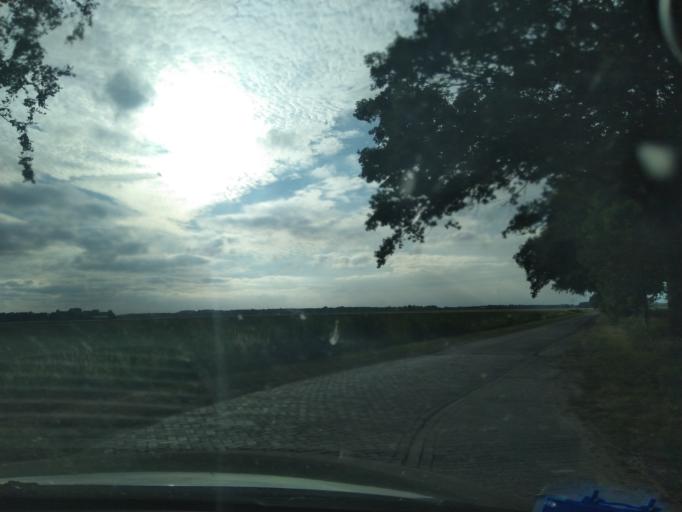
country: NL
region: Groningen
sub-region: Gemeente Vlagtwedde
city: Vlagtwedde
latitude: 53.0760
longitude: 7.1170
